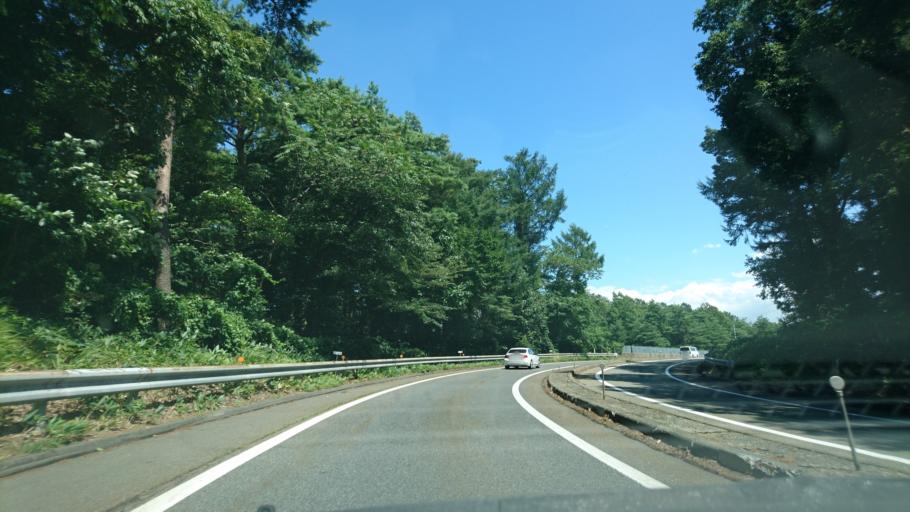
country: JP
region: Iwate
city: Morioka-shi
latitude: 39.7980
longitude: 141.1109
